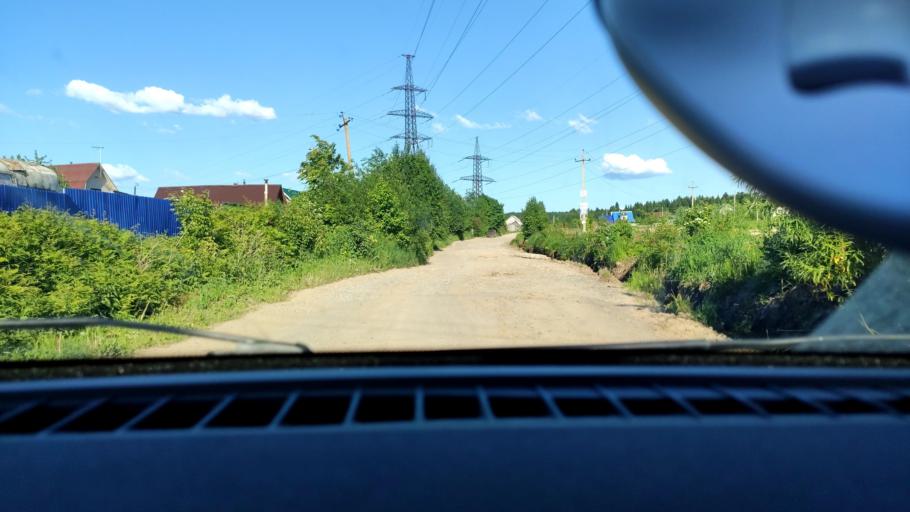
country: RU
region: Perm
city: Ferma
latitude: 57.9159
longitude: 56.3526
